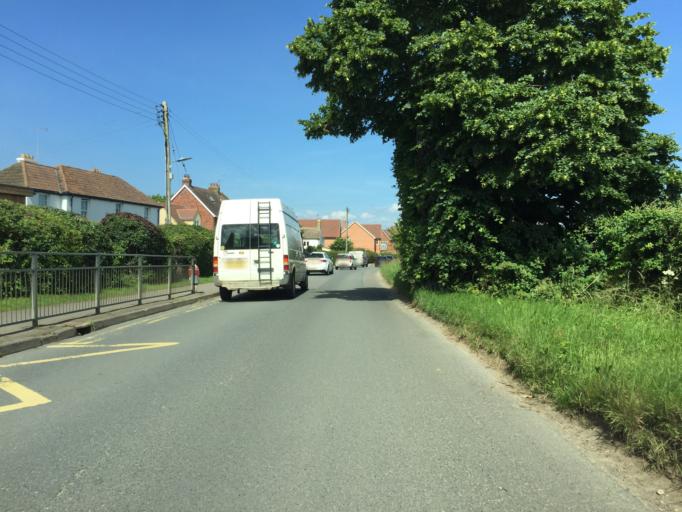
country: GB
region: England
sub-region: Gloucestershire
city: Dursley
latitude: 51.7242
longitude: -2.3734
